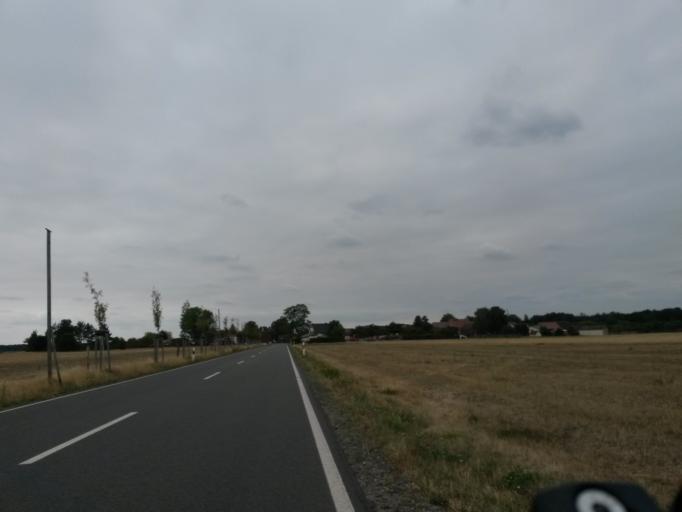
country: DE
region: Saxony-Anhalt
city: Muhlanger
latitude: 51.8704
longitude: 12.7860
